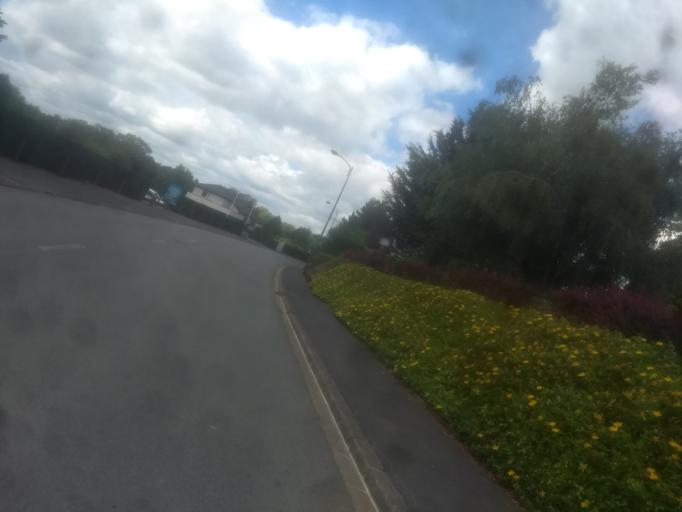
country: FR
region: Nord-Pas-de-Calais
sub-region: Departement du Pas-de-Calais
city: Anzin-Saint-Aubin
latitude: 50.3137
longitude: 2.7380
